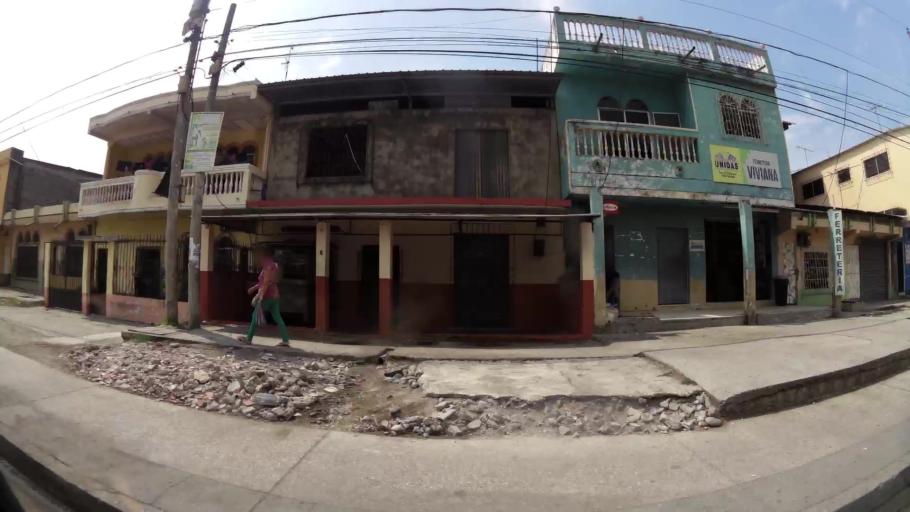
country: EC
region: Guayas
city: Guayaquil
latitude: -2.2454
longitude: -79.8905
